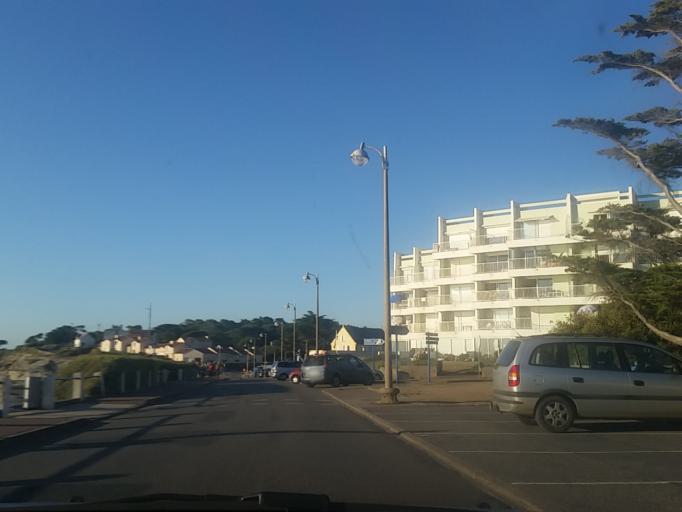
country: FR
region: Pays de la Loire
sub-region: Departement de la Loire-Atlantique
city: Saint-Michel-Chef-Chef
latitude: 47.1803
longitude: -2.1628
